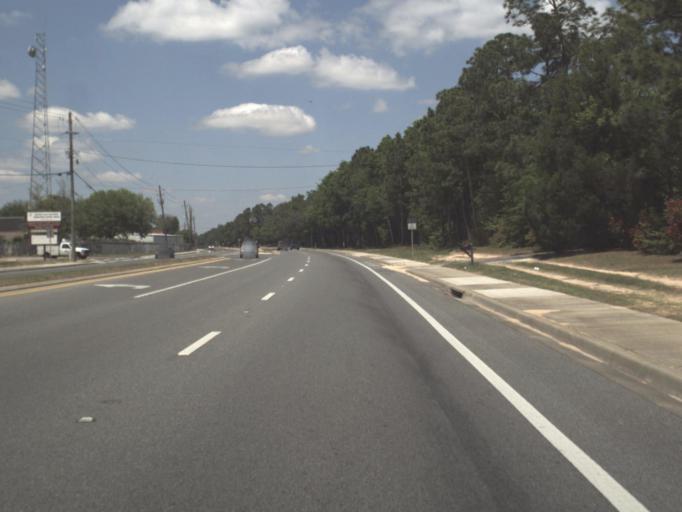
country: US
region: Florida
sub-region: Santa Rosa County
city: Milton
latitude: 30.6561
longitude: -87.0470
